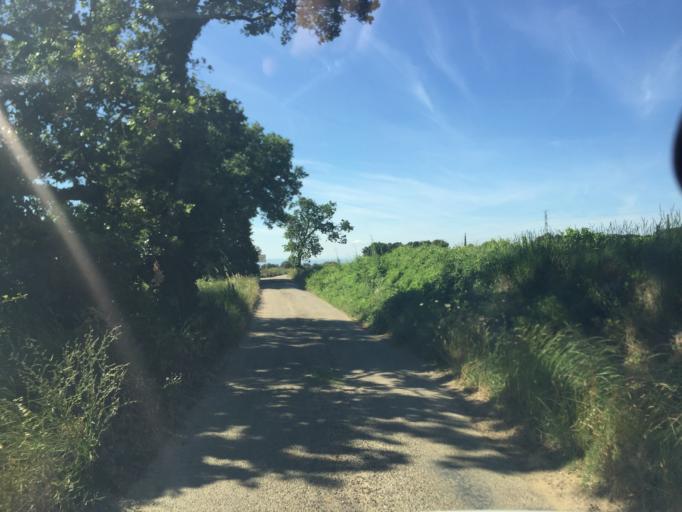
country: FR
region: Provence-Alpes-Cote d'Azur
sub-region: Departement du Vaucluse
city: Chateauneuf-du-Pape
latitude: 44.0854
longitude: 4.8058
